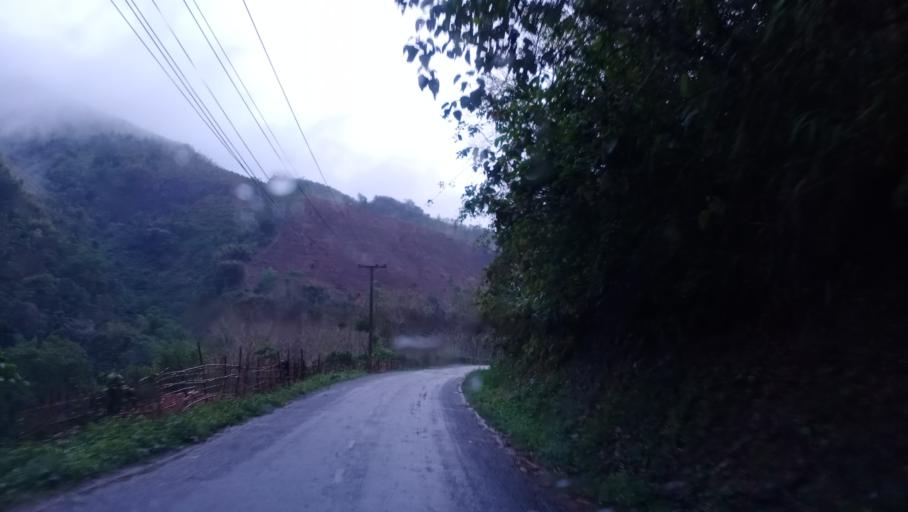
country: LA
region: Phongsali
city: Khoa
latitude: 21.0638
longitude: 102.4848
